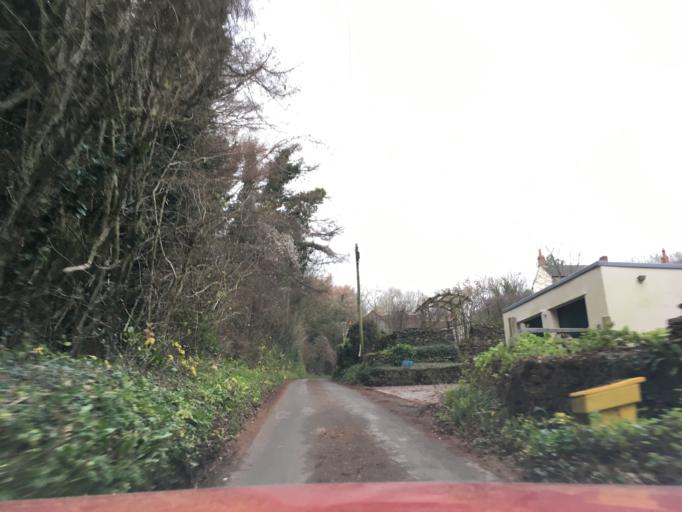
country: GB
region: Wales
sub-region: Monmouthshire
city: Rogiet
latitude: 51.5998
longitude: -2.7790
